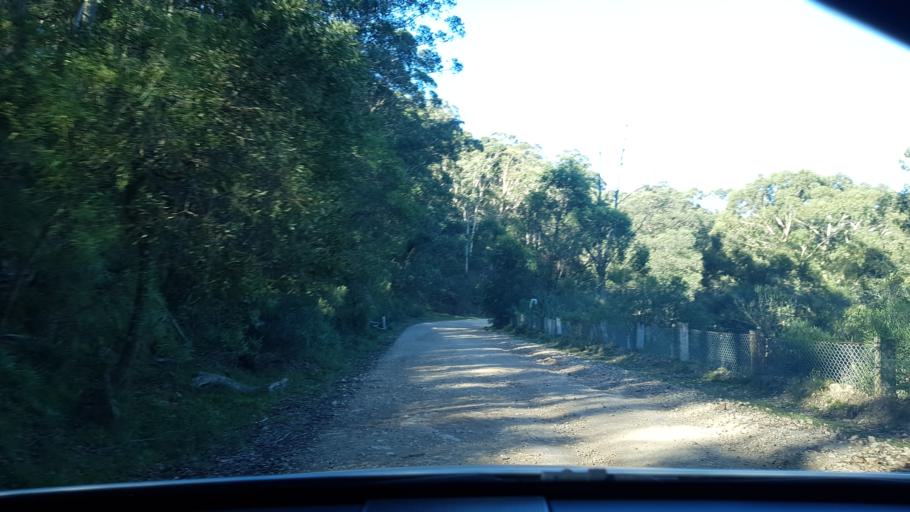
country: AU
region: New South Wales
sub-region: Oberon
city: Oberon
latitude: -33.8541
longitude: 150.0281
